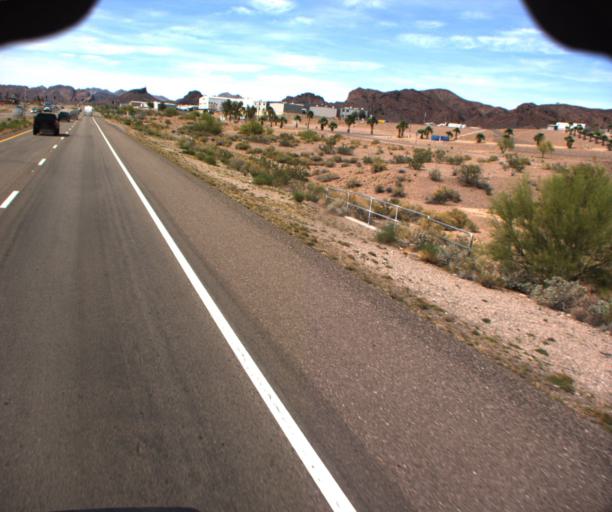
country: US
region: Arizona
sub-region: Mohave County
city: Desert Hills
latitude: 34.5646
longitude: -114.3616
